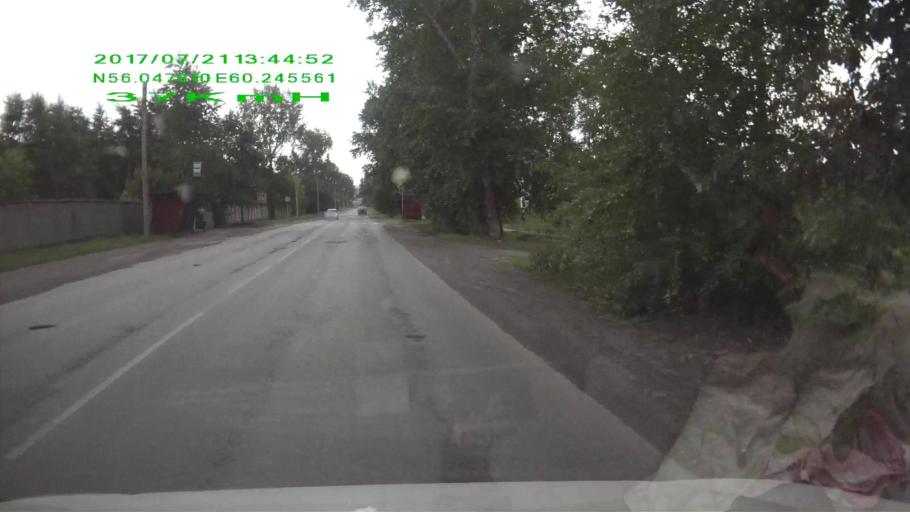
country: RU
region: Chelyabinsk
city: Verkhniy Ufaley
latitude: 56.0474
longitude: 60.2454
